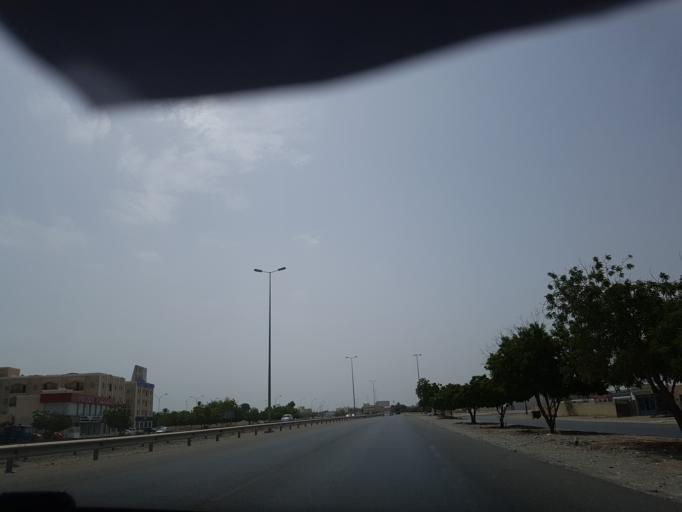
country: OM
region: Al Batinah
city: As Suwayq
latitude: 23.7493
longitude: 57.6149
